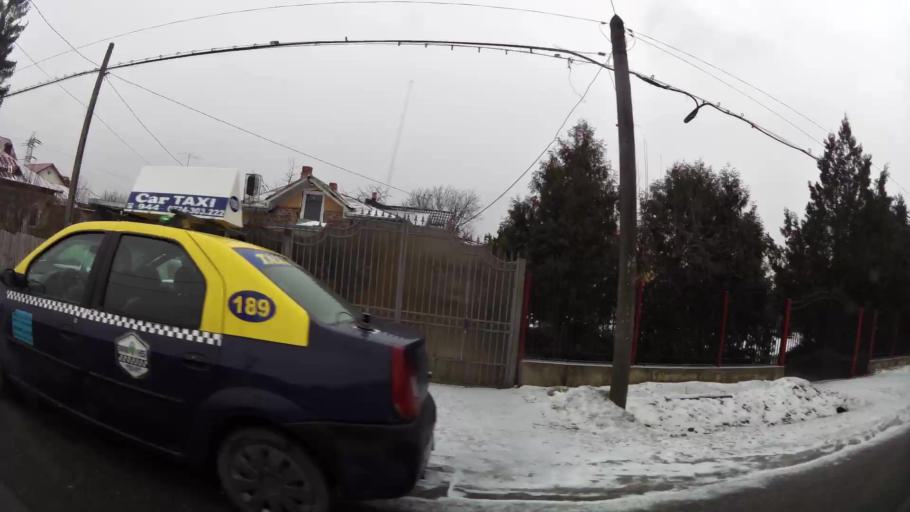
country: RO
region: Dambovita
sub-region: Municipiul Targoviste
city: Targoviste
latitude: 44.9370
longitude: 25.4899
